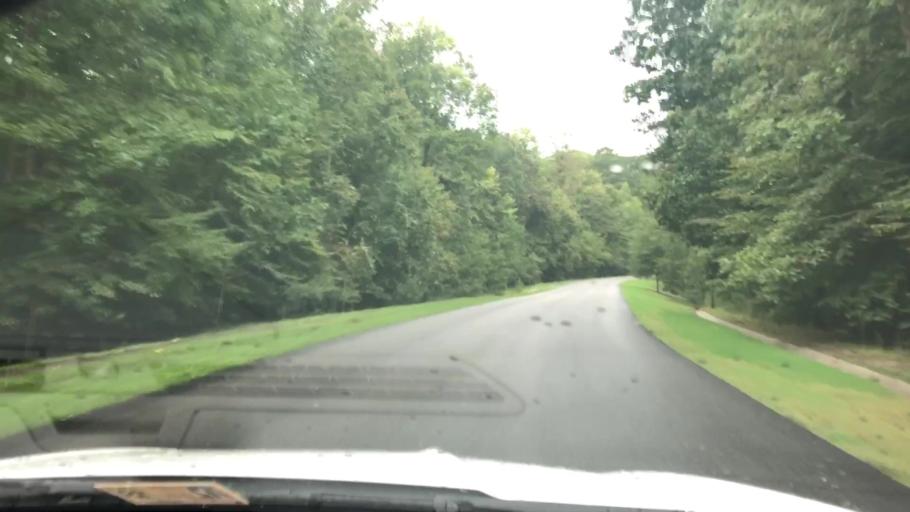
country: US
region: Virginia
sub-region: James City County
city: Williamsburg
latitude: 37.2795
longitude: -76.7730
